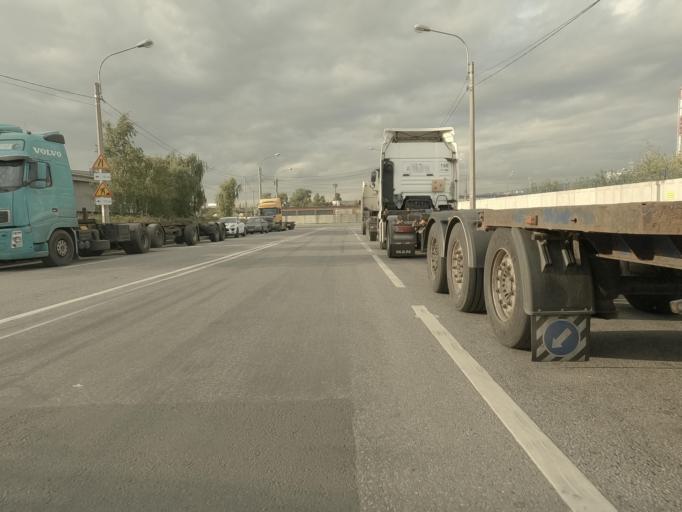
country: RU
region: St.-Petersburg
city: Avtovo
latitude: 59.8673
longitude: 30.2377
